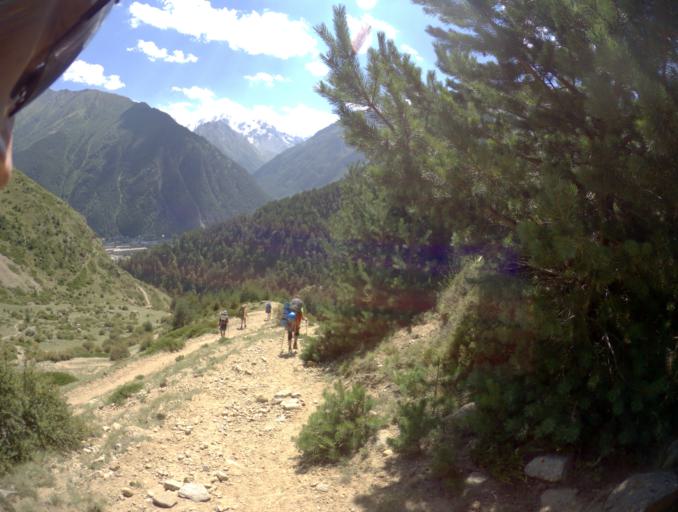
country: RU
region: Kabardino-Balkariya
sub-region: El'brusskiy Rayon
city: El'brus
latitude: 43.2656
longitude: 42.6348
